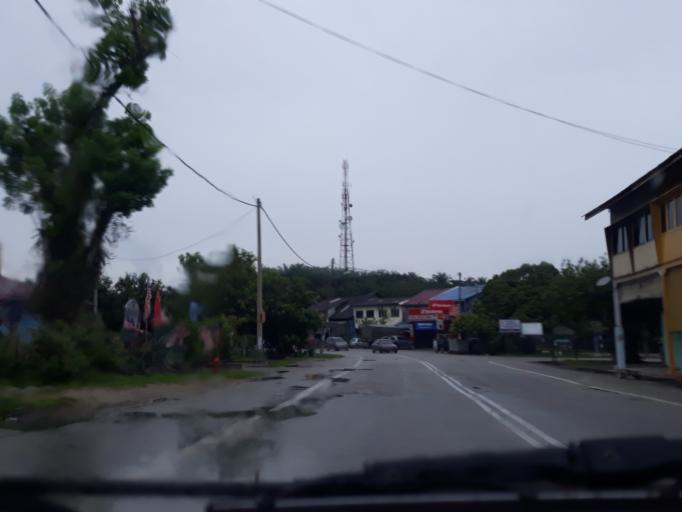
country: MY
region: Penang
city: Nibong Tebal
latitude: 5.2123
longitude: 100.6128
